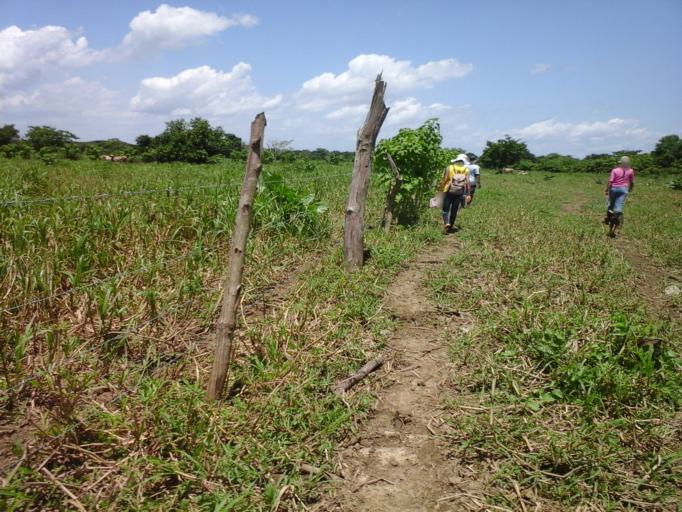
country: CO
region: Bolivar
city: Mahates
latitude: 10.1657
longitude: -75.2744
